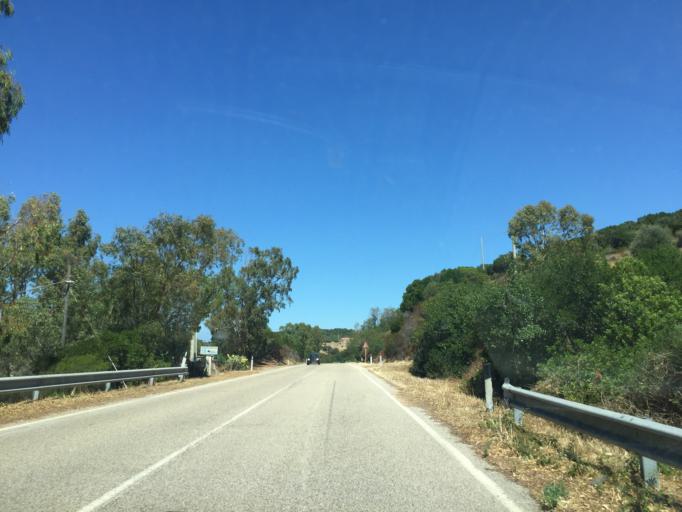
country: IT
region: Sardinia
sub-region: Provincia di Olbia-Tempio
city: Aglientu
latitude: 41.1019
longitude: 9.0842
